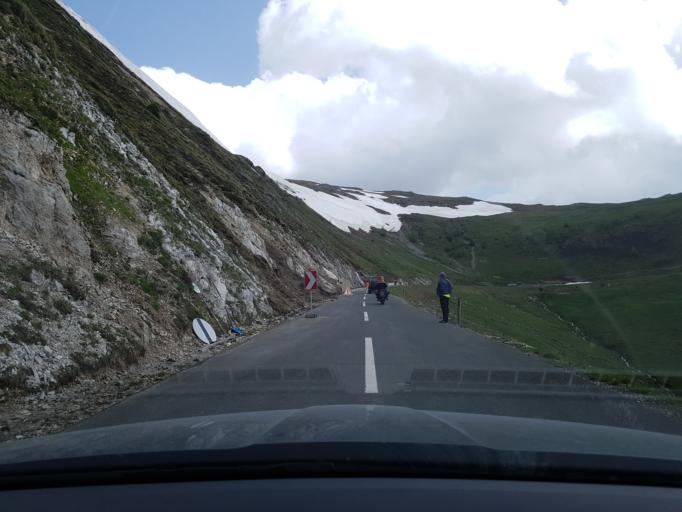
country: AT
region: Carinthia
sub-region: Politischer Bezirk Spittal an der Drau
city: Kleinkirchheim
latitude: 46.9377
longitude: 13.7546
